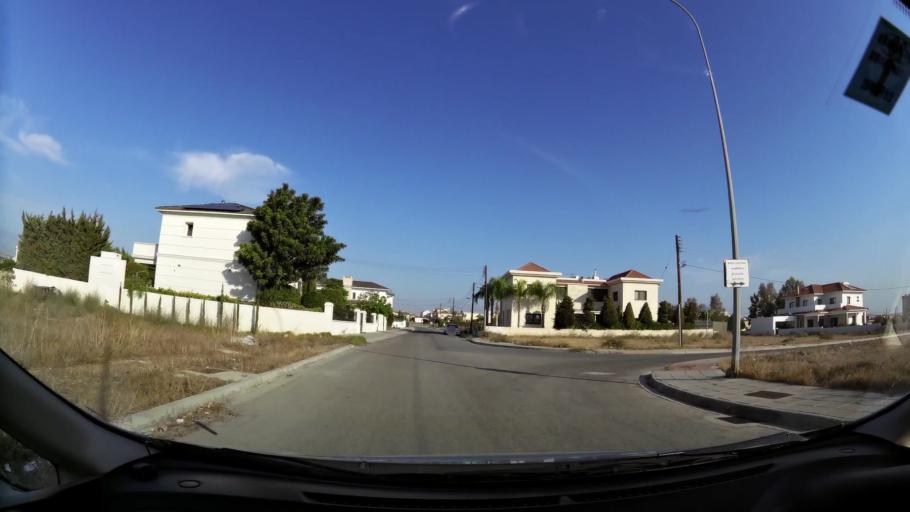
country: CY
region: Larnaka
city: Aradippou
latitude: 34.9349
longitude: 33.5960
